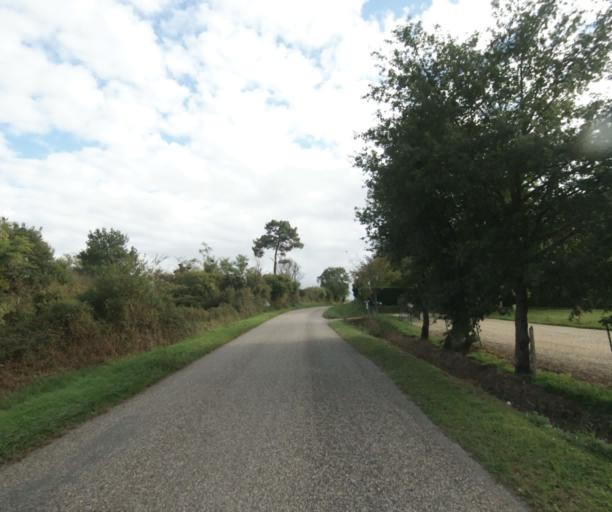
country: FR
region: Midi-Pyrenees
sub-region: Departement du Gers
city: Eauze
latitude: 43.8712
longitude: 0.1007
